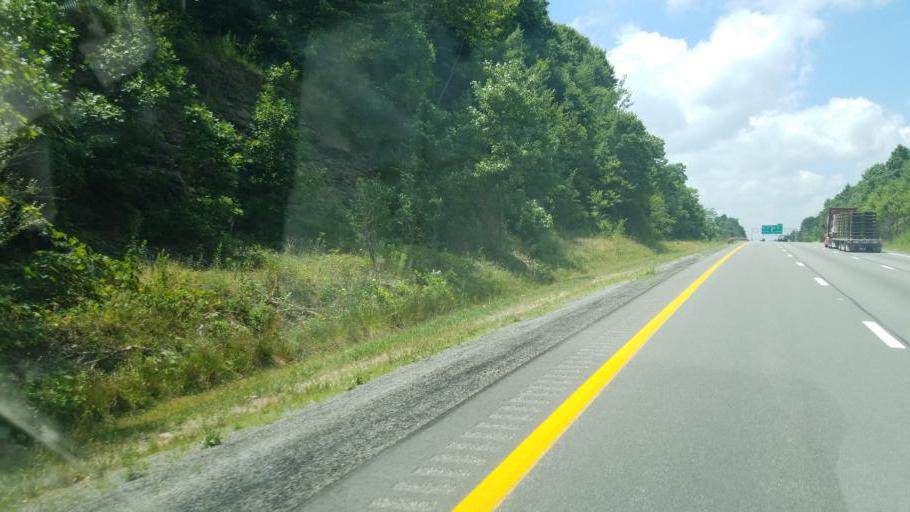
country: US
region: West Virginia
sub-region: Raleigh County
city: MacArthur
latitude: 37.7242
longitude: -81.1832
